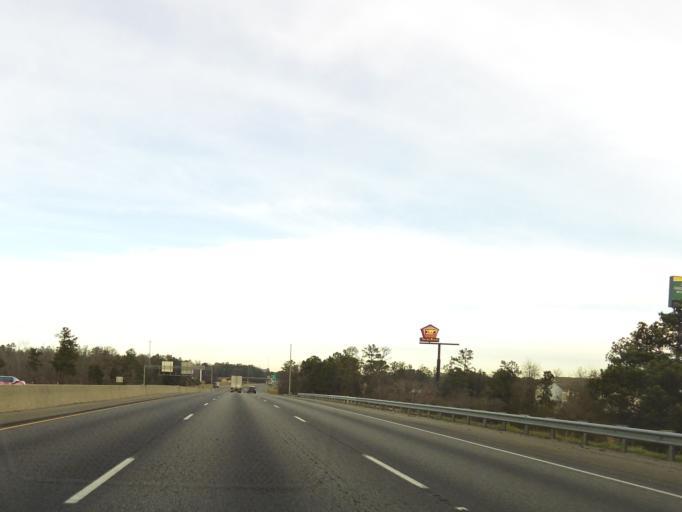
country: US
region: Georgia
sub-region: Bibb County
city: West Point
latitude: 32.8110
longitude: -83.7262
